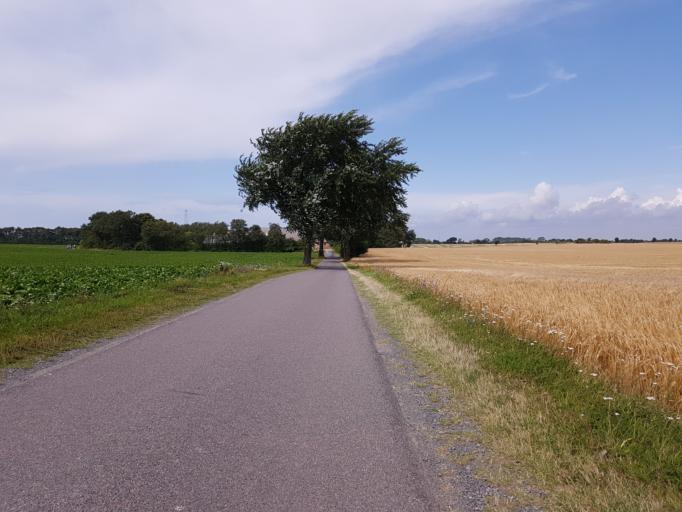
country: DK
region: Zealand
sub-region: Guldborgsund Kommune
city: Nykobing Falster
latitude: 54.5676
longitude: 11.9556
